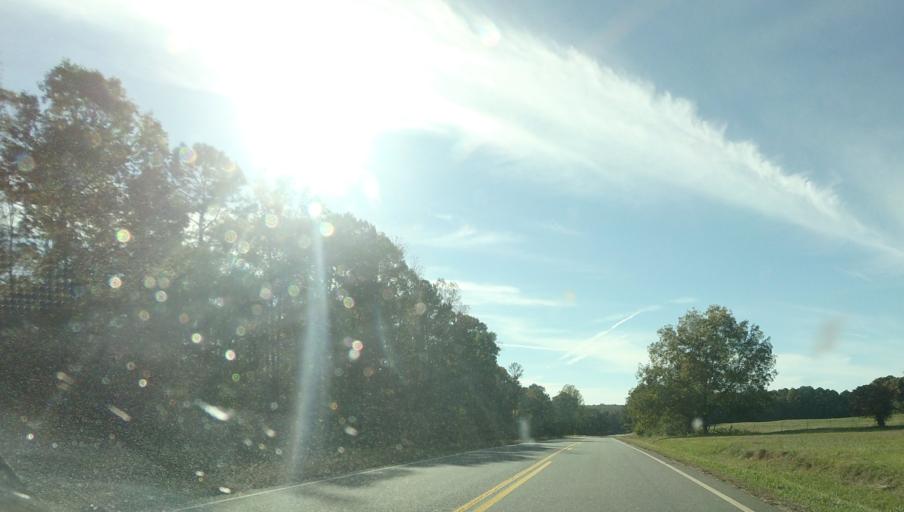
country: US
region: Georgia
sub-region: Talbot County
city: Talbotton
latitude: 32.6894
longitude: -84.4761
